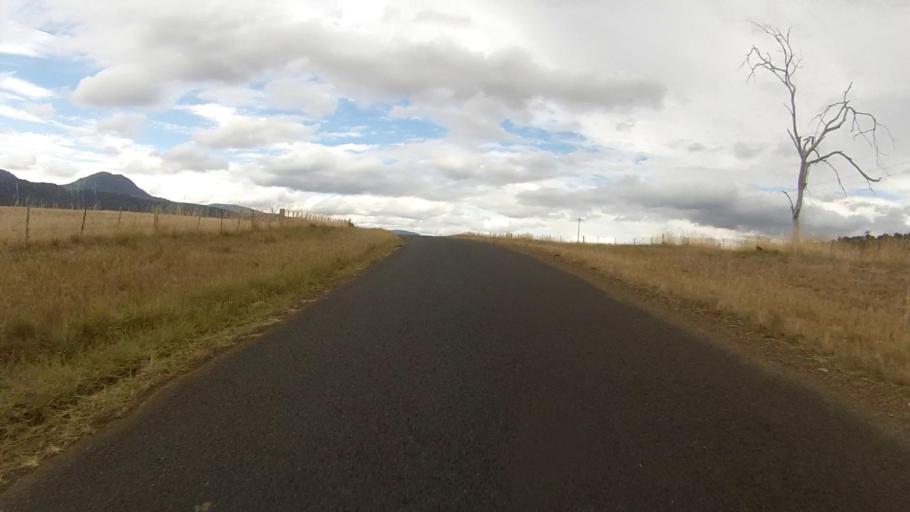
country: AU
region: Tasmania
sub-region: Northern Midlands
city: Evandale
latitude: -41.8275
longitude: 147.7887
